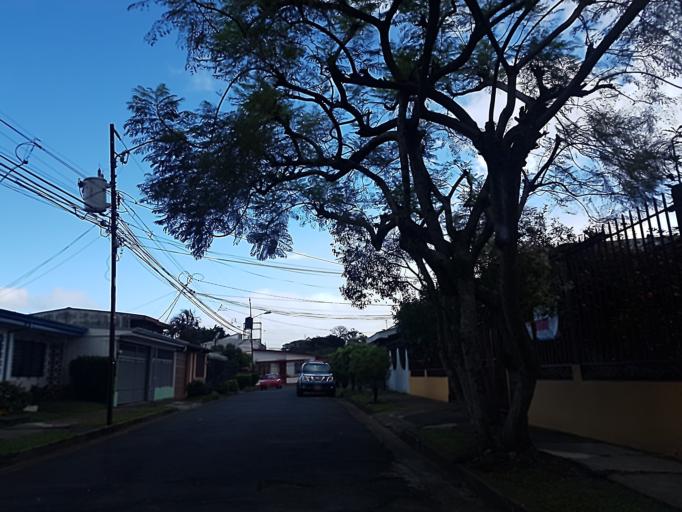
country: CR
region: San Jose
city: San Pedro
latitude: 9.9083
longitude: -84.0574
